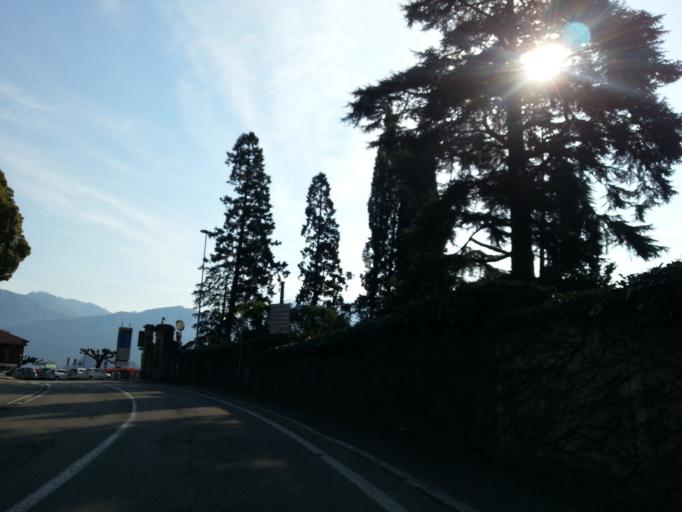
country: IT
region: Lombardy
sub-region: Provincia di Como
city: Tremezzo
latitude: 45.9817
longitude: 9.2210
